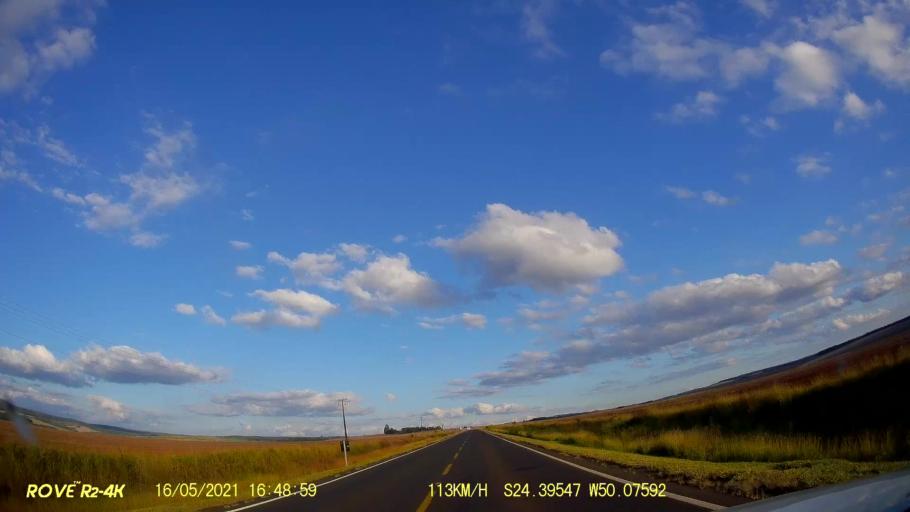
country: BR
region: Parana
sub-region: Pirai Do Sul
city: Pirai do Sul
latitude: -24.3956
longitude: -50.0758
